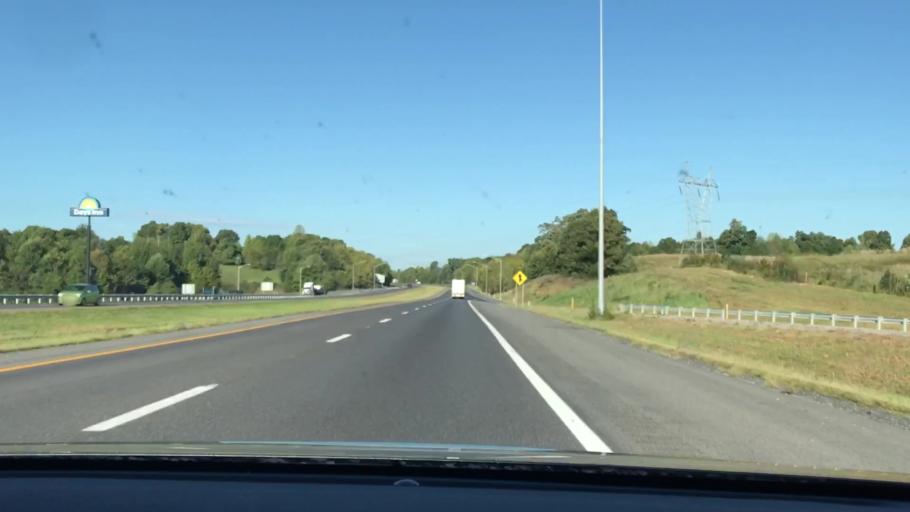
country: US
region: Kentucky
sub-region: Lyon County
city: Eddyville
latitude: 37.0746
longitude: -88.1236
